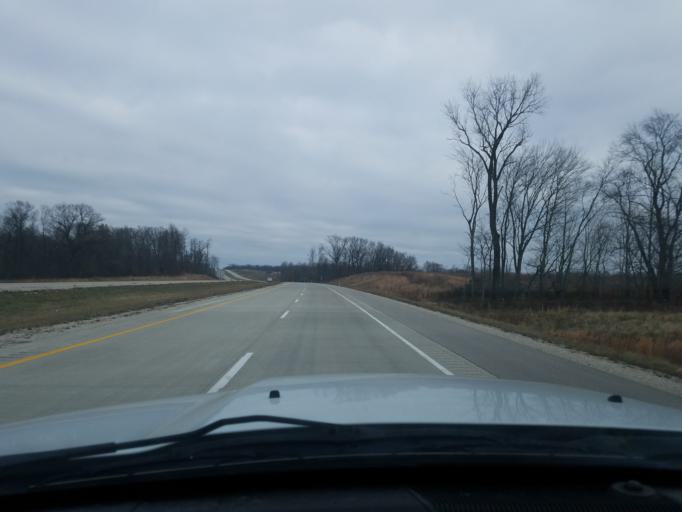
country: US
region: Indiana
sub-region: Greene County
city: Bloomfield
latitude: 38.9292
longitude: -86.8821
